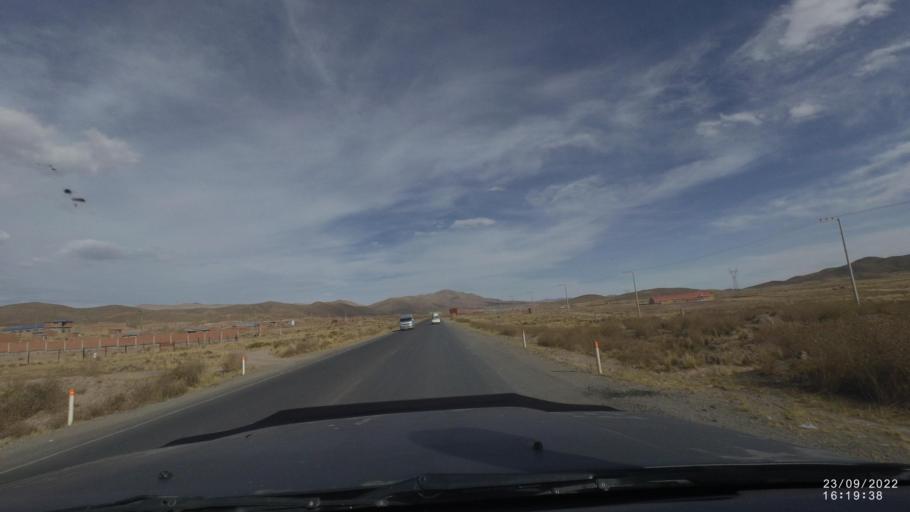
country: BO
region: Oruro
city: Oruro
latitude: -18.0275
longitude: -67.0235
